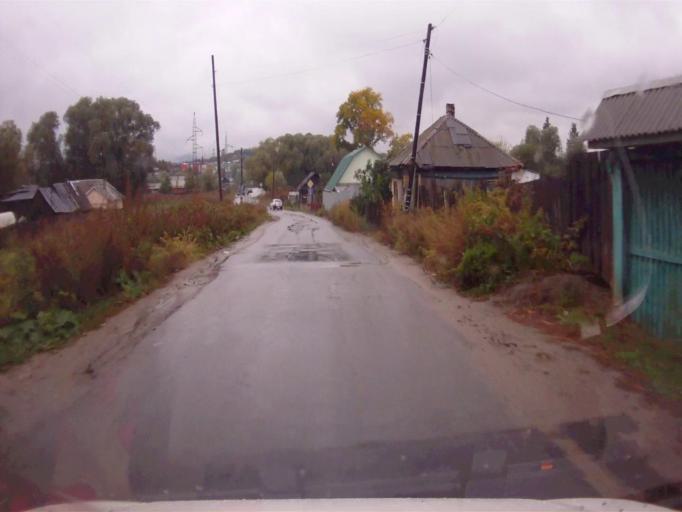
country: RU
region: Chelyabinsk
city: Kyshtym
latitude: 55.7149
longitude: 60.5486
